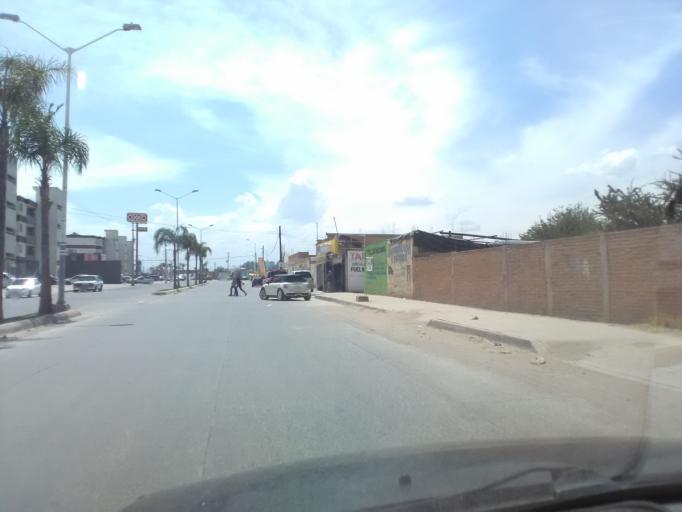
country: MX
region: Durango
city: Victoria de Durango
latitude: 24.0131
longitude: -104.6140
